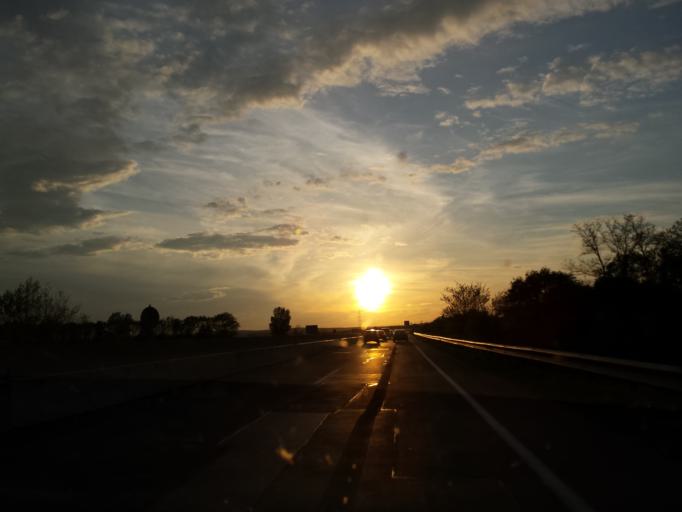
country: AT
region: Burgenland
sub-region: Politischer Bezirk Neusiedl am See
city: Parndorf
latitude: 47.9719
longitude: 16.8645
